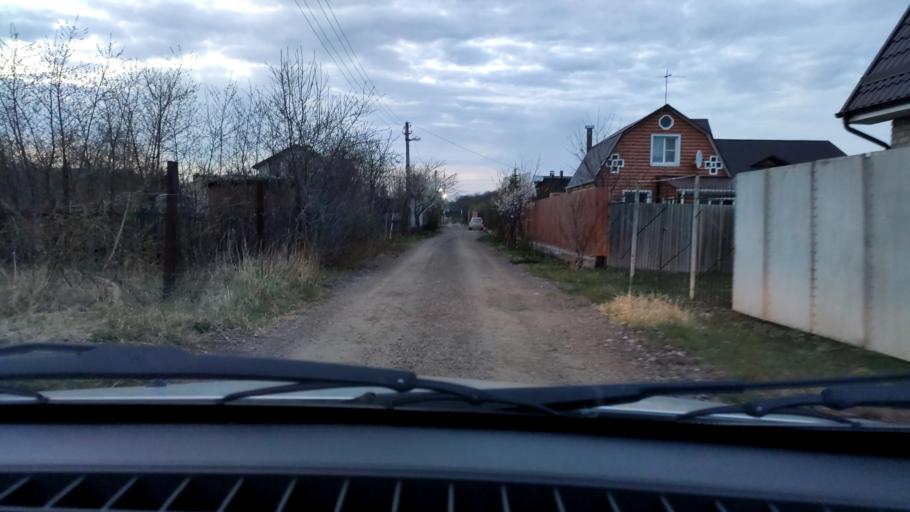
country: RU
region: Voronezj
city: Podgornoye
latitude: 51.7978
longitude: 39.2227
